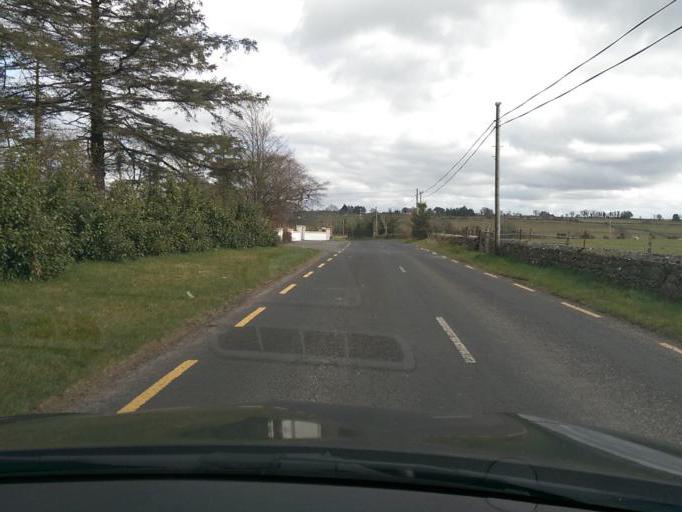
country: IE
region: Connaught
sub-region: County Galway
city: Loughrea
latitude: 53.4190
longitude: -8.5214
